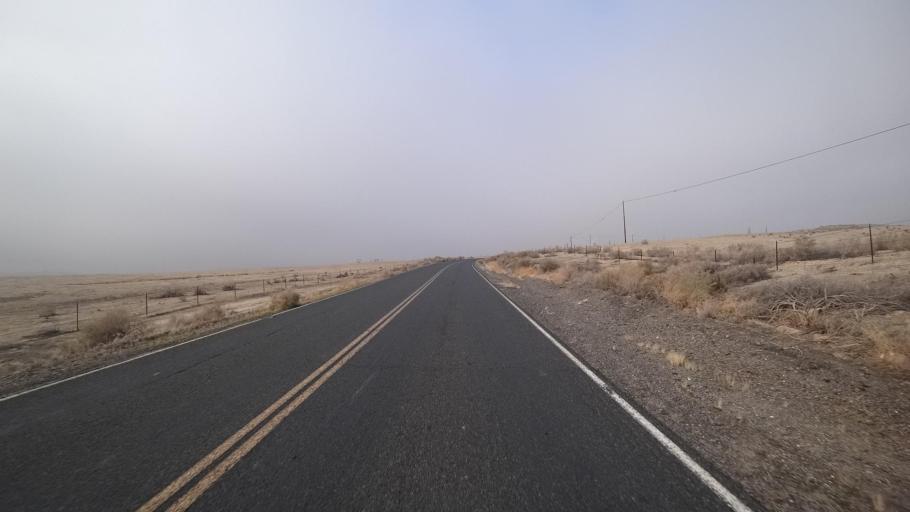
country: US
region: California
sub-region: Kern County
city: Ford City
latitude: 35.2509
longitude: -119.4635
